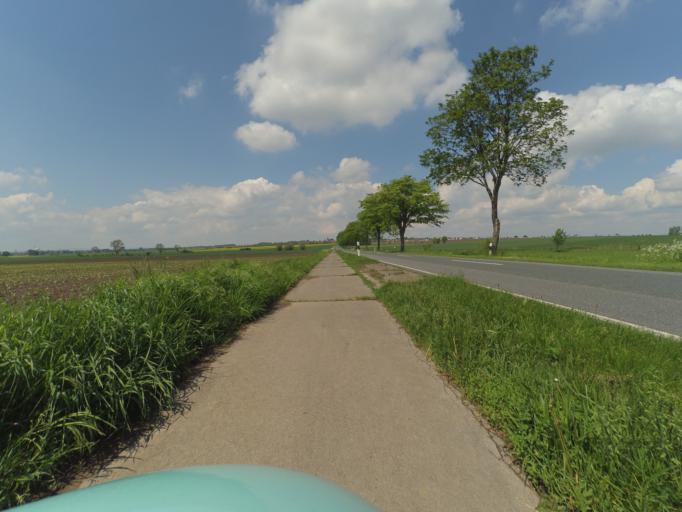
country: DE
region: Lower Saxony
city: Hohenhameln
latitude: 52.2521
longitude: 10.0919
